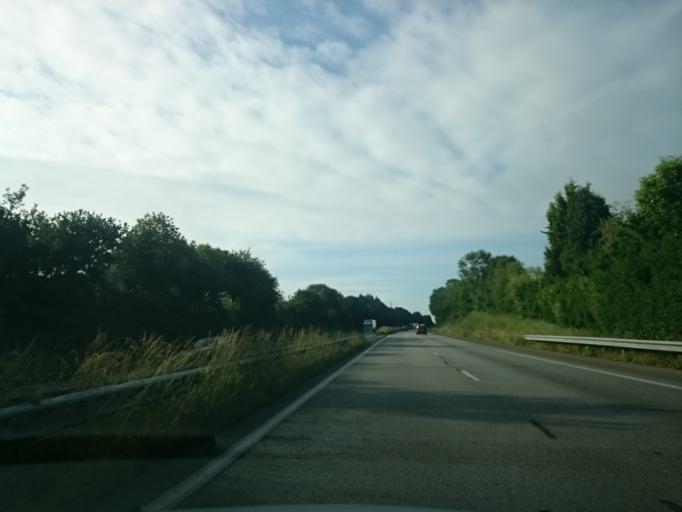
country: FR
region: Brittany
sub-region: Departement du Finistere
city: Briec
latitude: 48.1320
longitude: -4.0250
